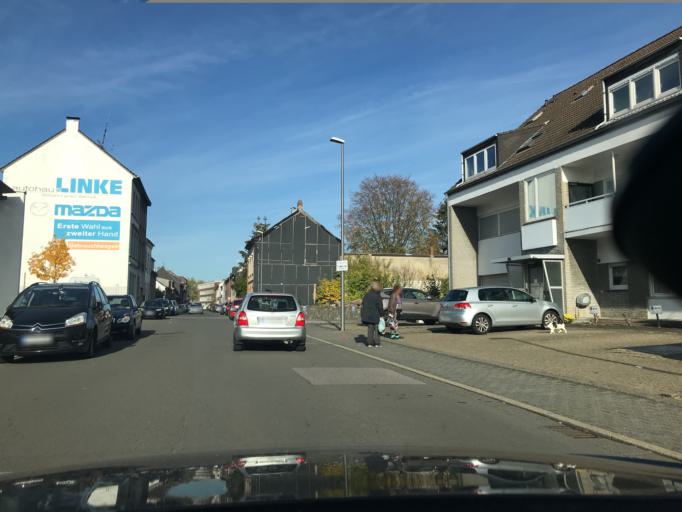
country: DE
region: North Rhine-Westphalia
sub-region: Regierungsbezirk Dusseldorf
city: Krefeld
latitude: 51.3214
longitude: 6.5858
